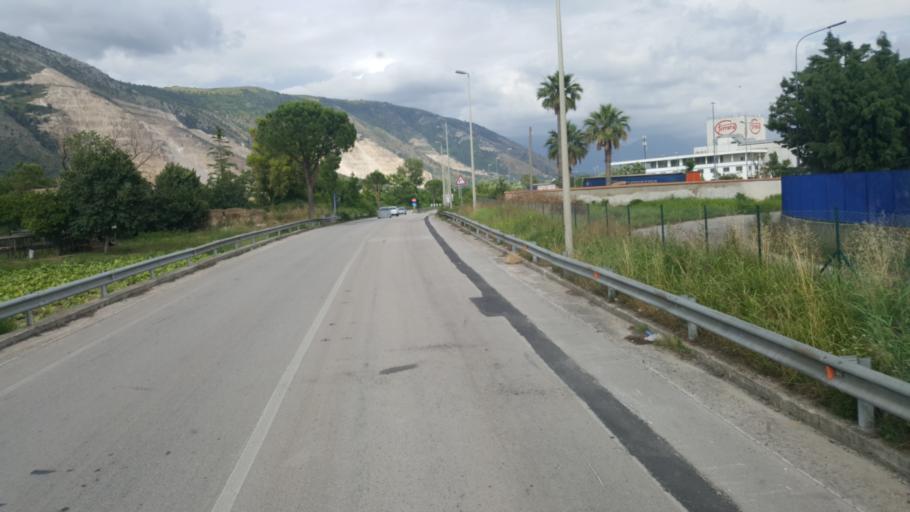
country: IT
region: Campania
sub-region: Provincia di Caserta
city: San Felice A Cancello
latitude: 40.9786
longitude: 14.4659
